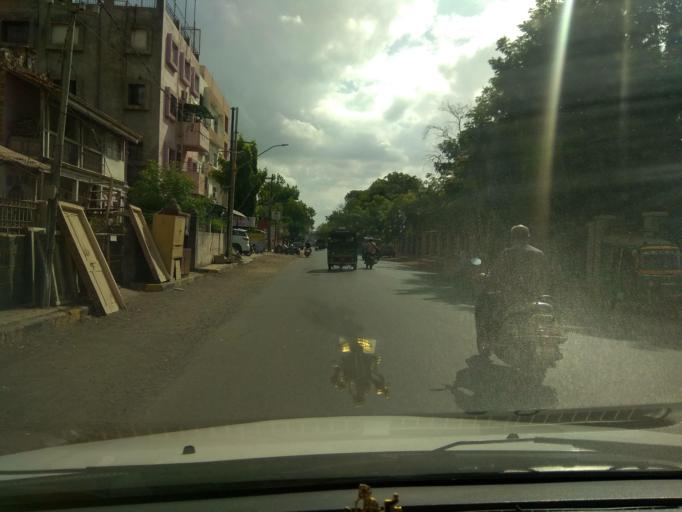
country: IN
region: Gujarat
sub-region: Bhavnagar
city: Bhavnagar
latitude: 21.7720
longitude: 72.1399
